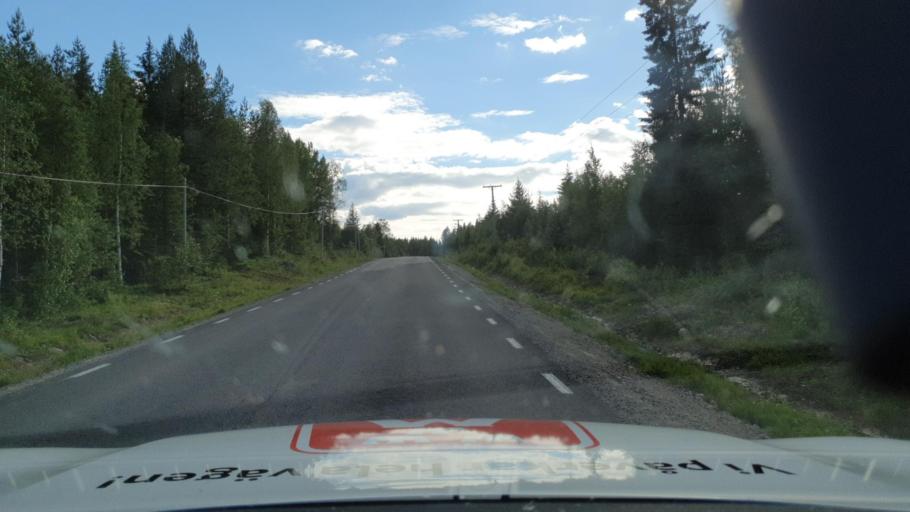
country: SE
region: Vaesterbotten
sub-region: Skelleftea Kommun
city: Langsele
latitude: 64.7682
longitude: 19.9985
